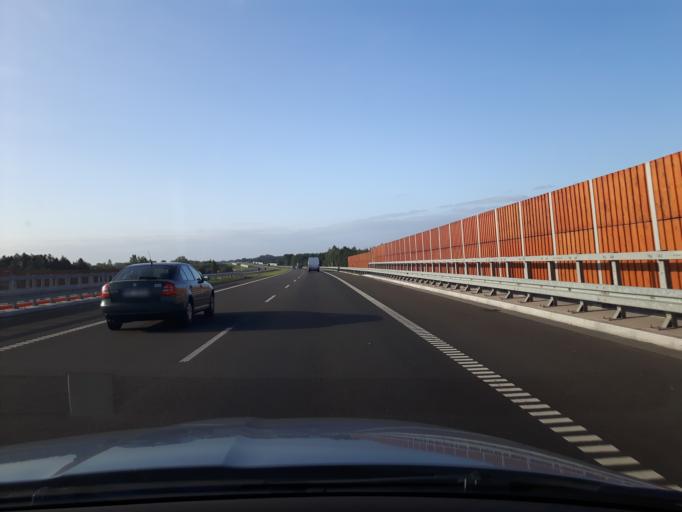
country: PL
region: Masovian Voivodeship
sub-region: Powiat radomski
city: Wolanow
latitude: 51.3648
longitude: 21.0140
